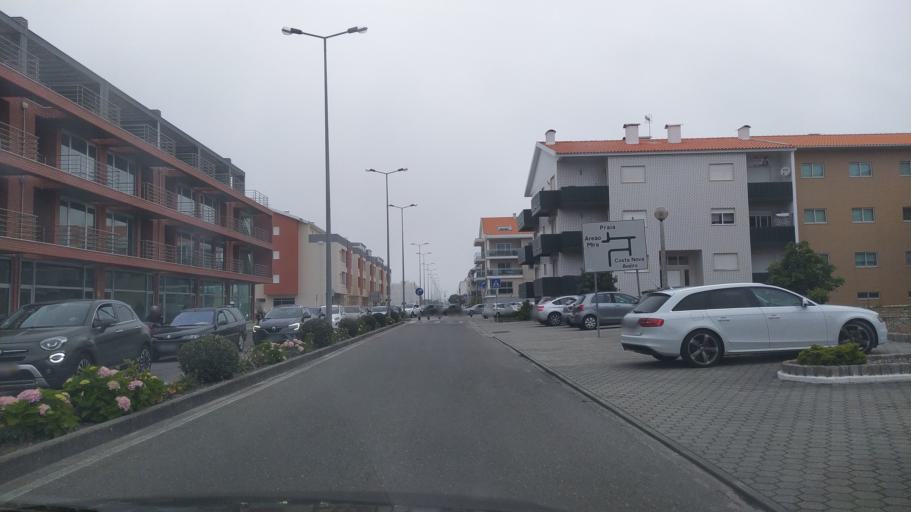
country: PT
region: Aveiro
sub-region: Ilhavo
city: Gafanha da Encarnacao
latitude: 40.5613
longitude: -8.7611
